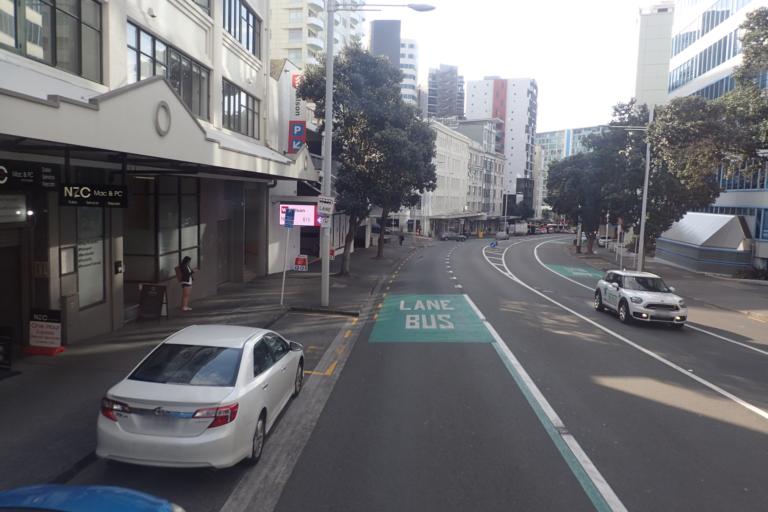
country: NZ
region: Auckland
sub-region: Auckland
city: Auckland
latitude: -36.8476
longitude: 174.7725
